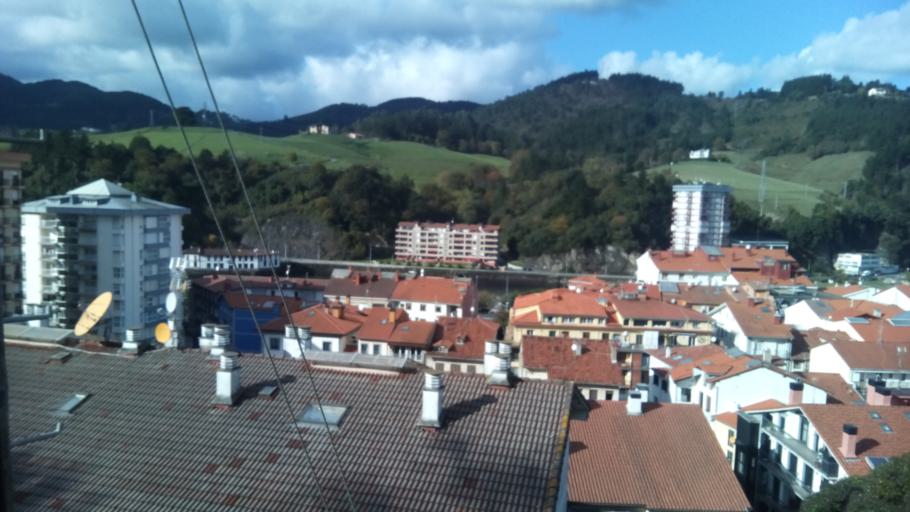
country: ES
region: Basque Country
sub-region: Provincia de Guipuzcoa
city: Deba
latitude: 43.2932
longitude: -2.3532
